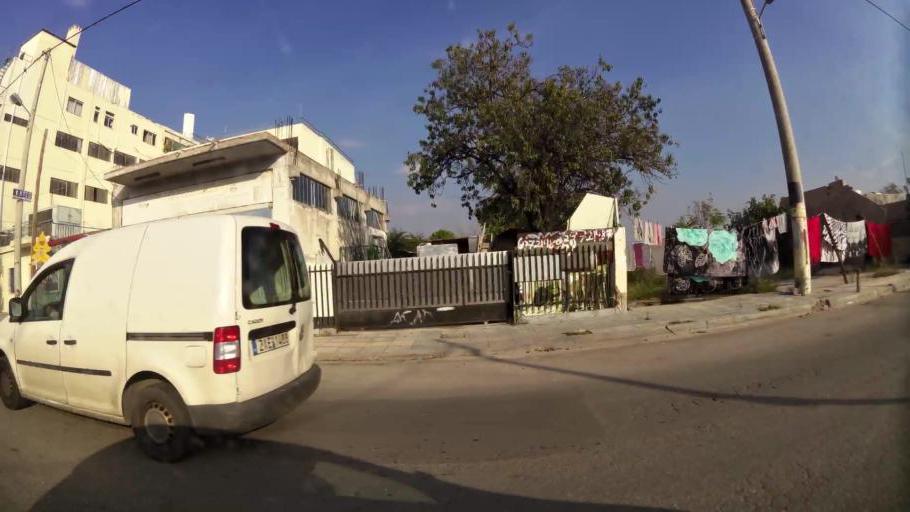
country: GR
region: Attica
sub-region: Nomarchia Anatolikis Attikis
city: Acharnes
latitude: 38.0795
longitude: 23.7453
